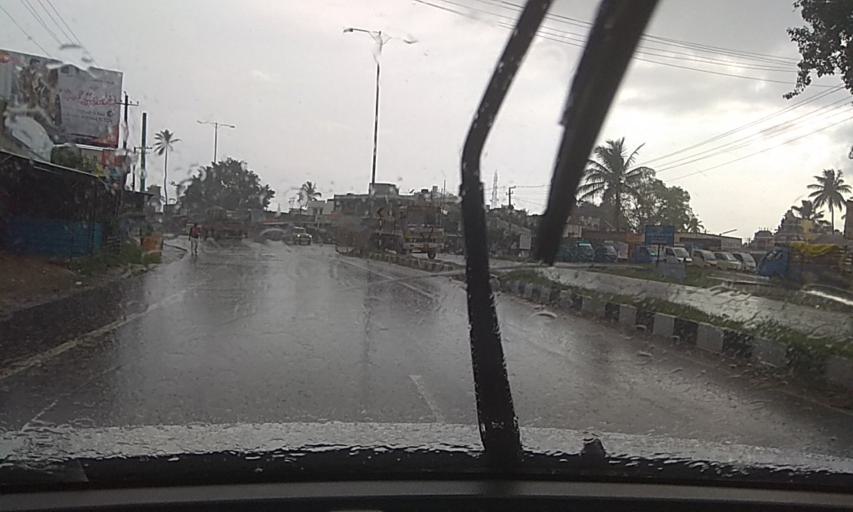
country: IN
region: Karnataka
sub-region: Mysore
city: Nanjangud
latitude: 12.1932
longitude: 76.6662
